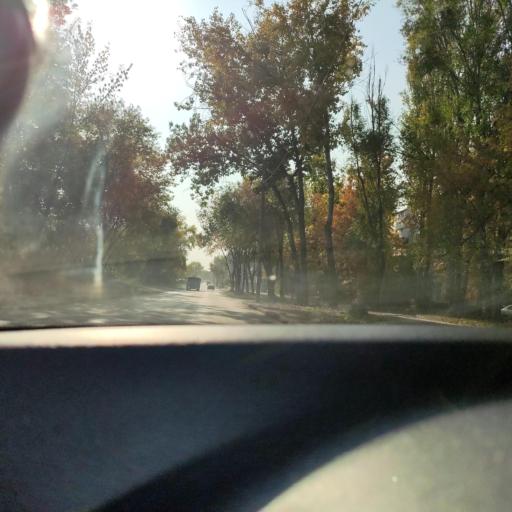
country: RU
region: Samara
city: Samara
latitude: 53.2240
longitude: 50.2086
